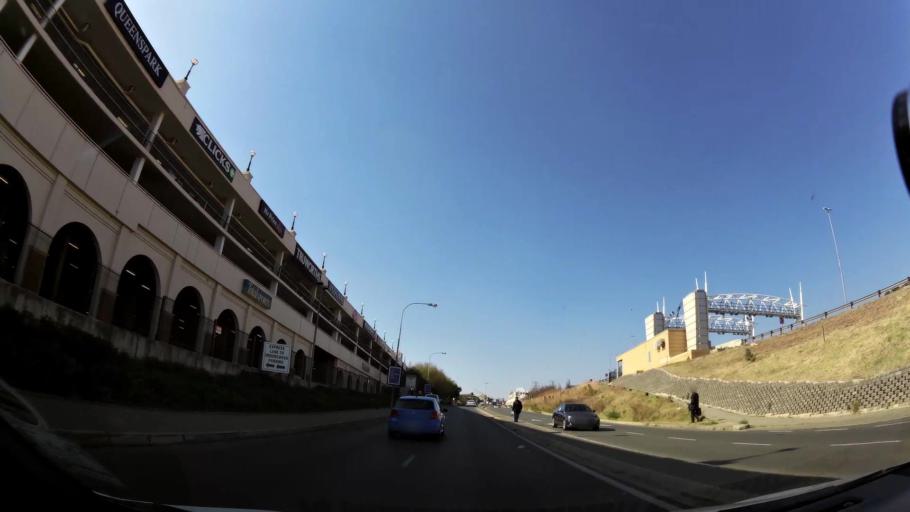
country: ZA
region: Gauteng
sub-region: City of Johannesburg Metropolitan Municipality
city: Johannesburg
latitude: -26.2693
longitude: 28.0488
